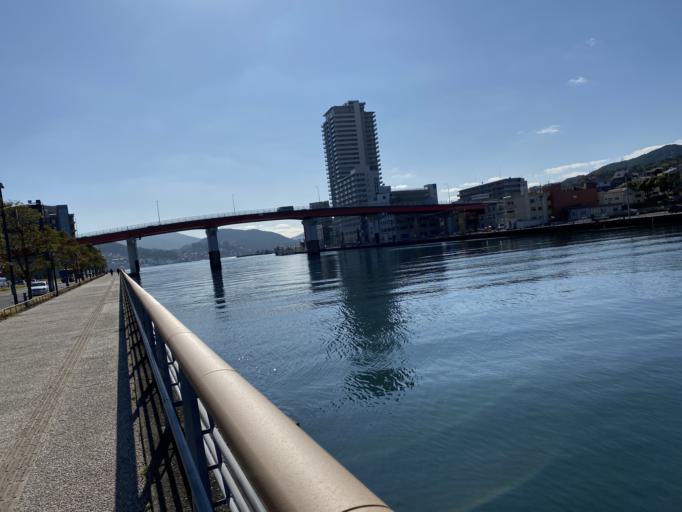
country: JP
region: Nagasaki
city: Nagasaki-shi
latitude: 32.7533
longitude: 129.8669
